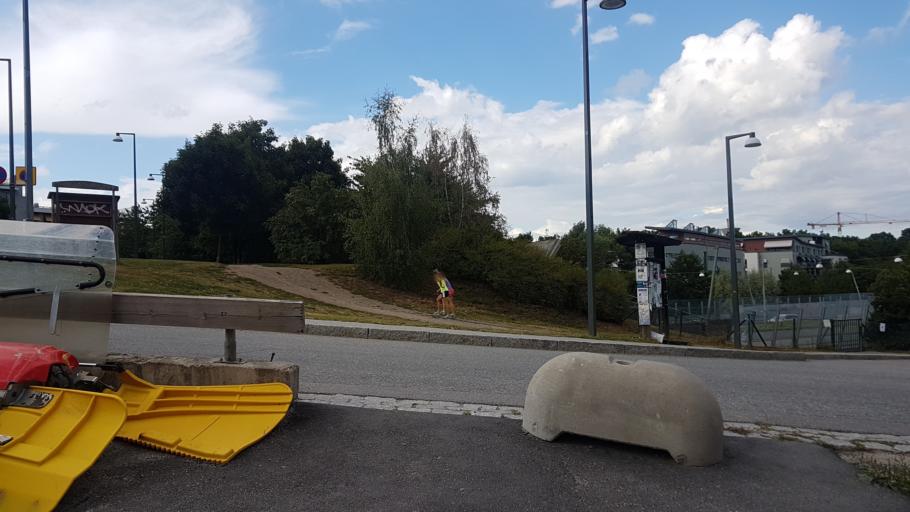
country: SE
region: Stockholm
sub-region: Stockholms Kommun
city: OEstermalm
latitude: 59.3012
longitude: 18.1092
